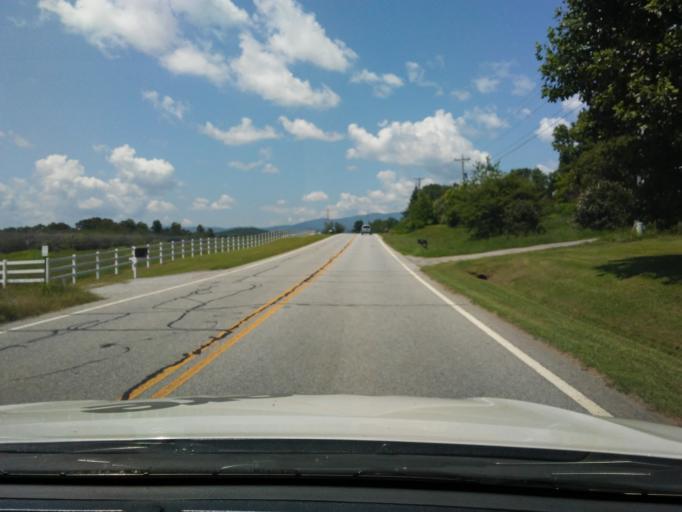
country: US
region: Georgia
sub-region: Towns County
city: Hiawassee
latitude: 34.9844
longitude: -83.7550
